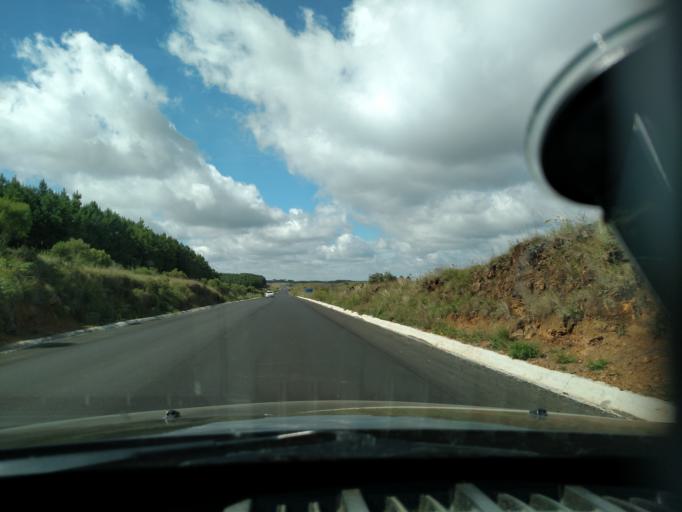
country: BR
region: Santa Catarina
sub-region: Lages
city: Lages
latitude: -28.0037
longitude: -50.0868
